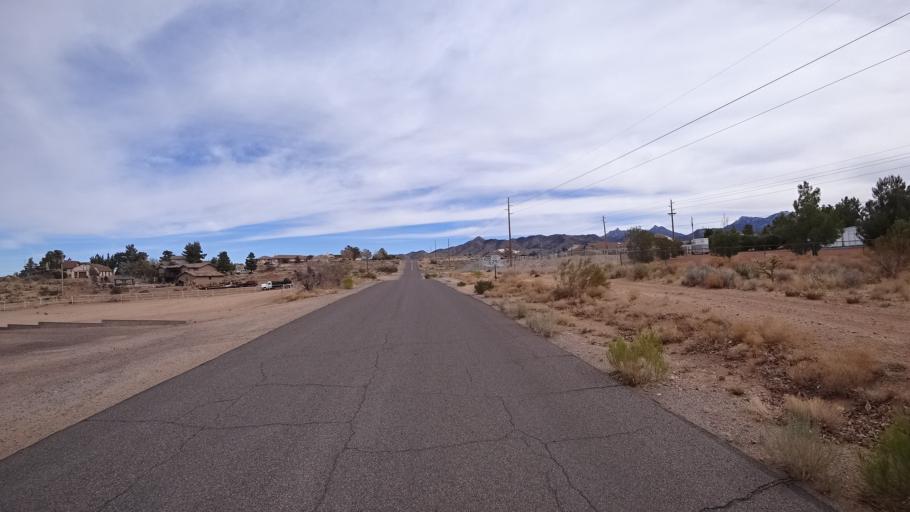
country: US
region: Arizona
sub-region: Mohave County
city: Kingman
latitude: 35.1814
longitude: -113.9922
